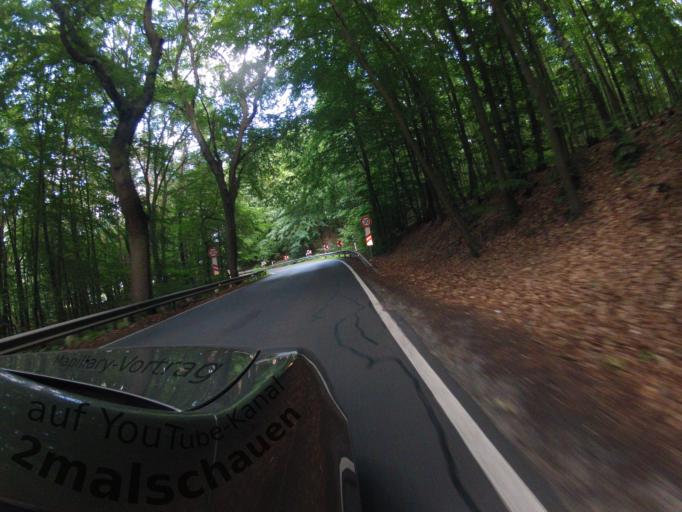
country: DE
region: Mecklenburg-Vorpommern
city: Seebad Heringsdorf
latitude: 53.9322
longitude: 14.1897
